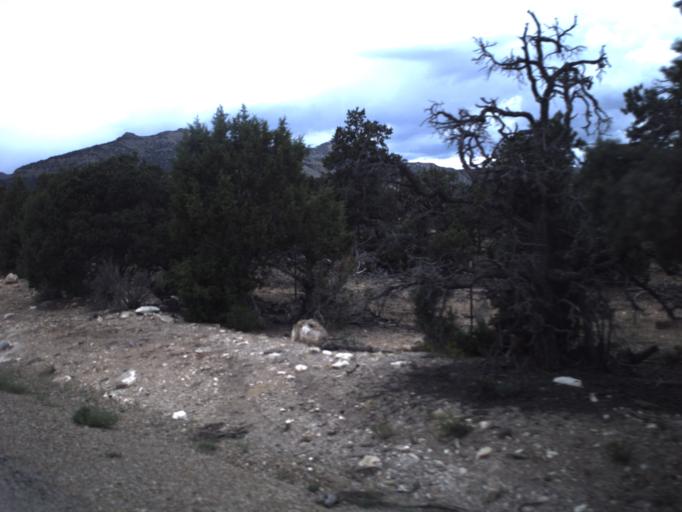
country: US
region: Utah
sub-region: Emery County
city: Huntington
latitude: 39.4842
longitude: -110.9720
